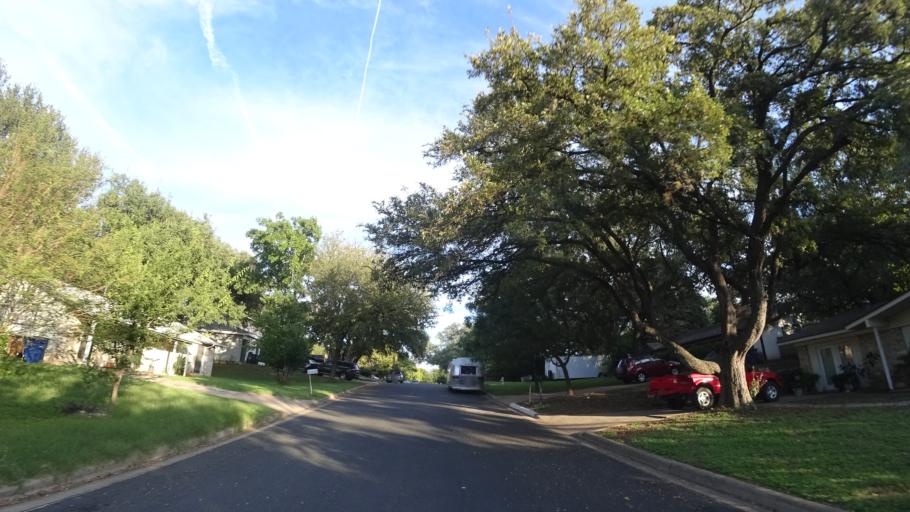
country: US
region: Texas
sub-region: Travis County
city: Austin
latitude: 30.2131
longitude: -97.7660
